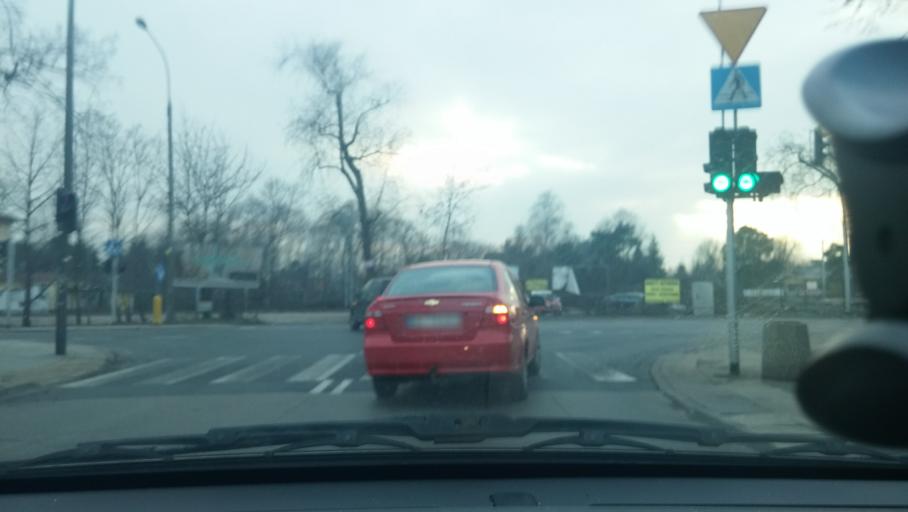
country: PL
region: Masovian Voivodeship
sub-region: Warszawa
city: Rembertow
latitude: 52.2253
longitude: 21.1493
